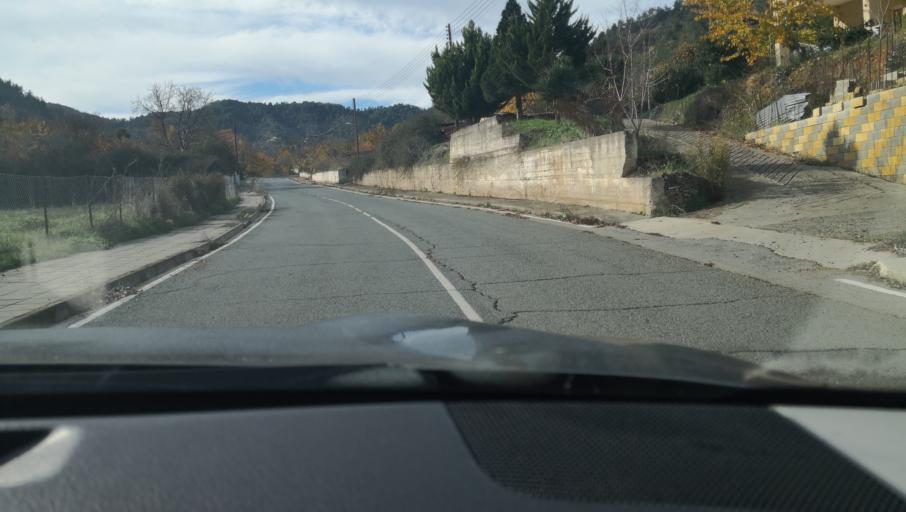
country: CY
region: Lefkosia
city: Lefka
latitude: 35.0337
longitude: 32.7316
